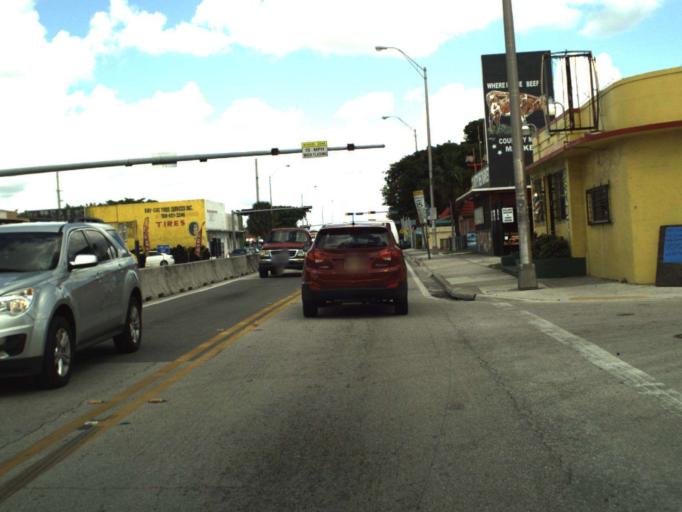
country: US
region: Florida
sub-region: Miami-Dade County
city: Allapattah
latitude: 25.8341
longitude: -80.2085
